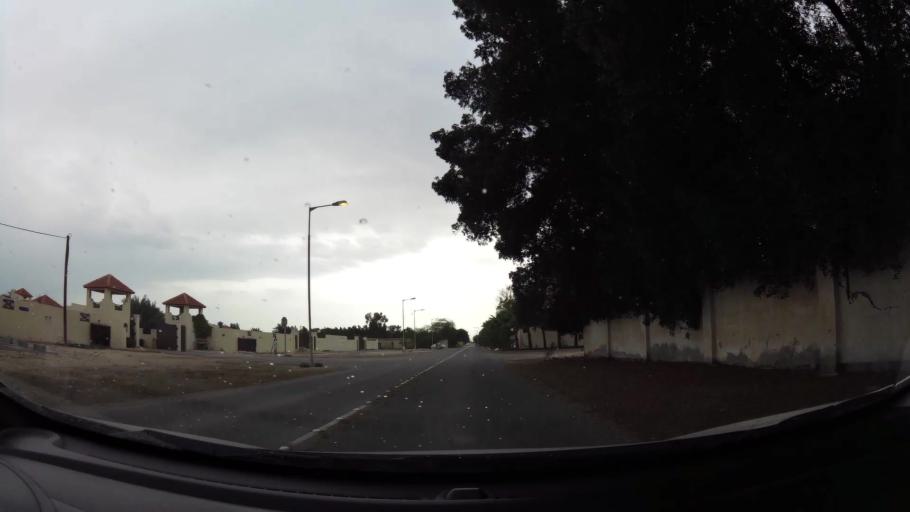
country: BH
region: Central Governorate
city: Madinat Hamad
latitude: 26.1577
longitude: 50.4611
